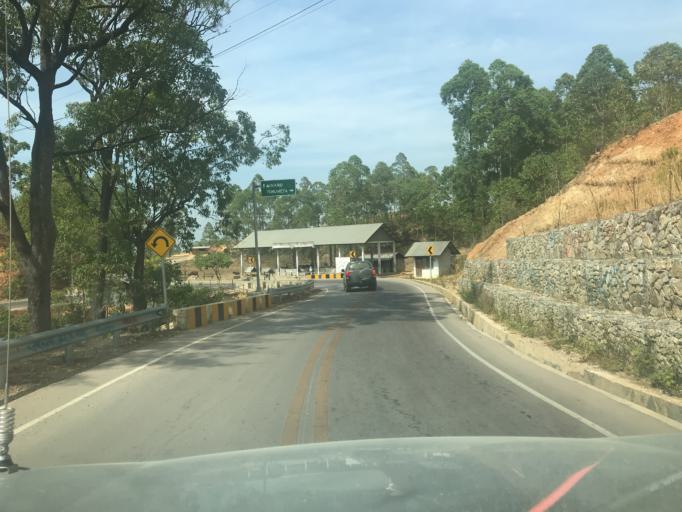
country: TL
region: Aileu
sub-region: Aileu Villa
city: Aileu
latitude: -8.6575
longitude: 125.5607
